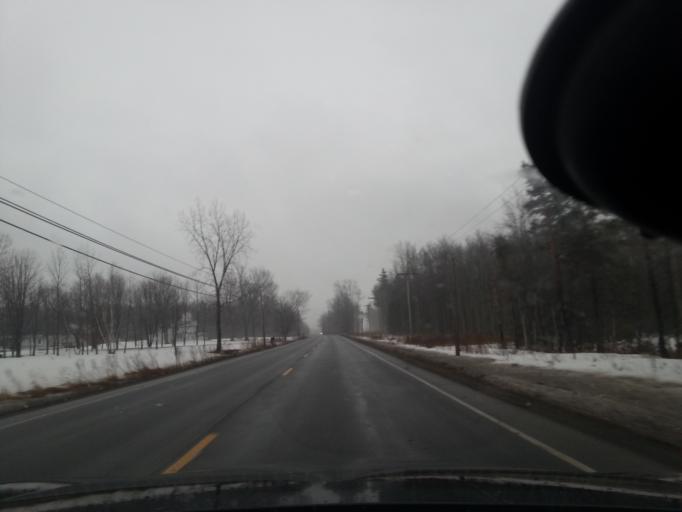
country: US
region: New York
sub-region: St. Lawrence County
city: Ogdensburg
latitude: 44.6487
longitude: -75.4413
